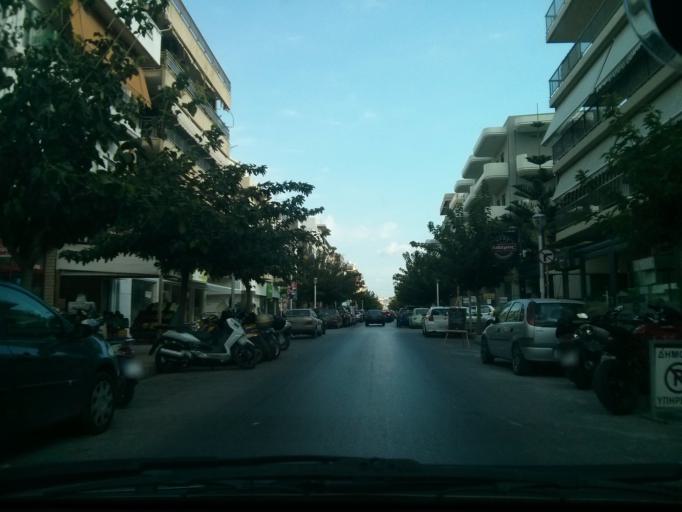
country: GR
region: Crete
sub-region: Nomos Irakleiou
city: Irakleion
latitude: 35.3318
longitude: 25.1352
